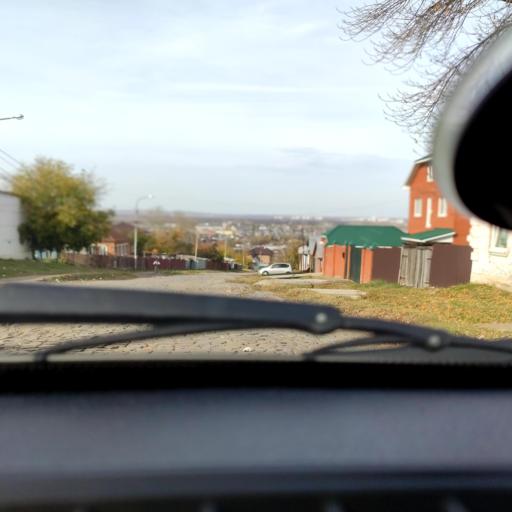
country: RU
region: Bashkortostan
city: Ufa
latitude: 54.7280
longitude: 55.9204
